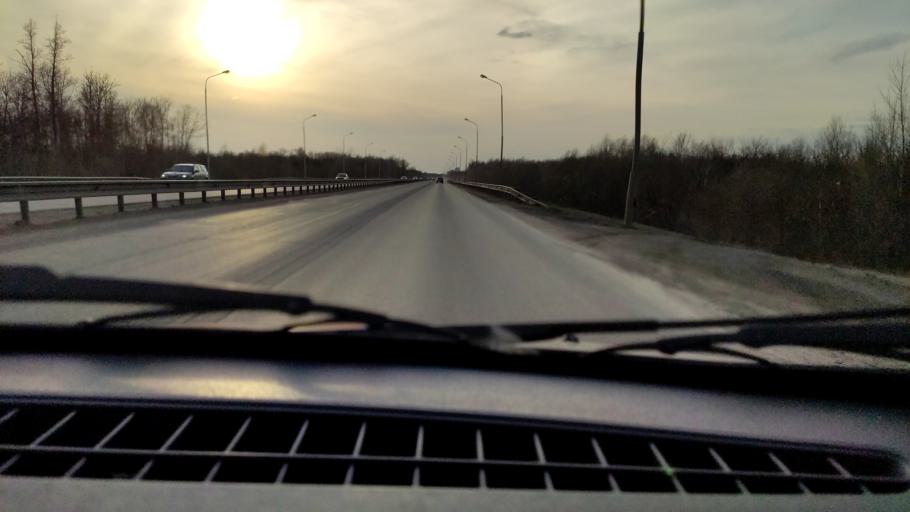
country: RU
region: Bashkortostan
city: Ufa
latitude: 54.6678
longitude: 56.0572
